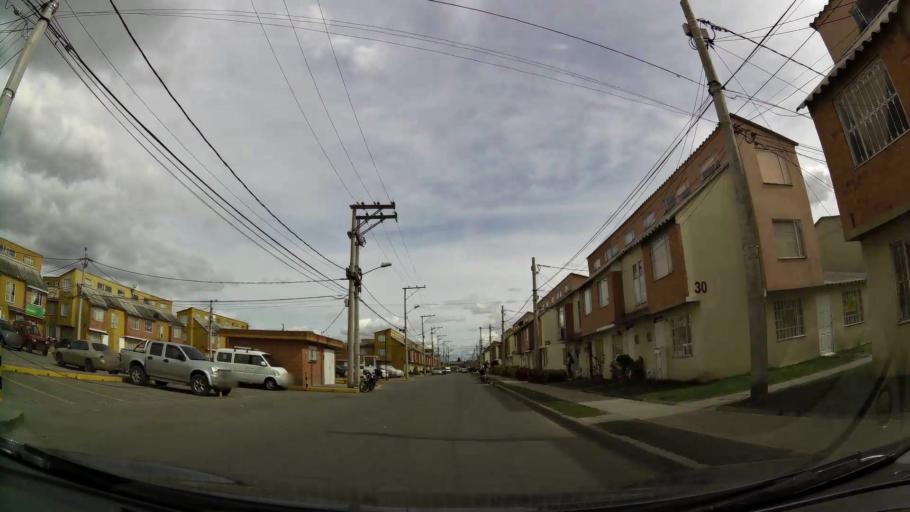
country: CO
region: Cundinamarca
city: Funza
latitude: 4.7118
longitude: -74.2002
